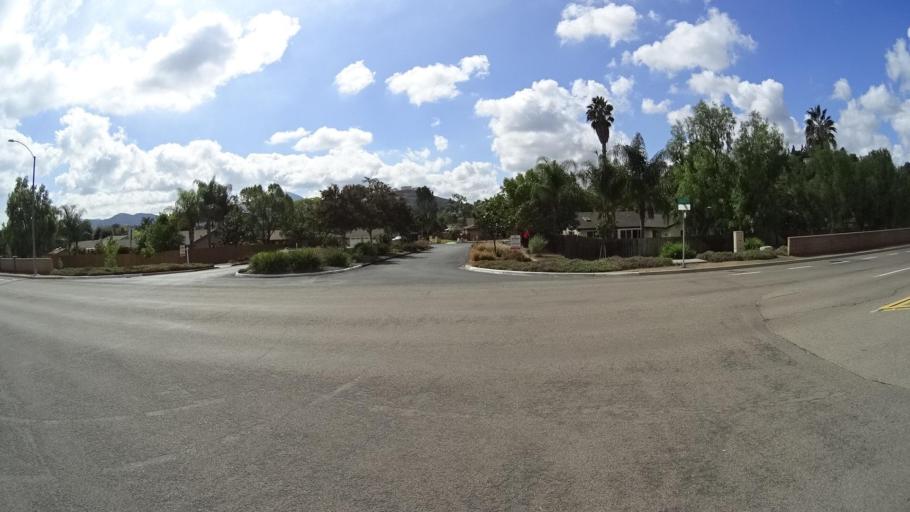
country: US
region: California
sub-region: San Diego County
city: Rancho San Diego
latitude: 32.7685
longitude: -116.9260
